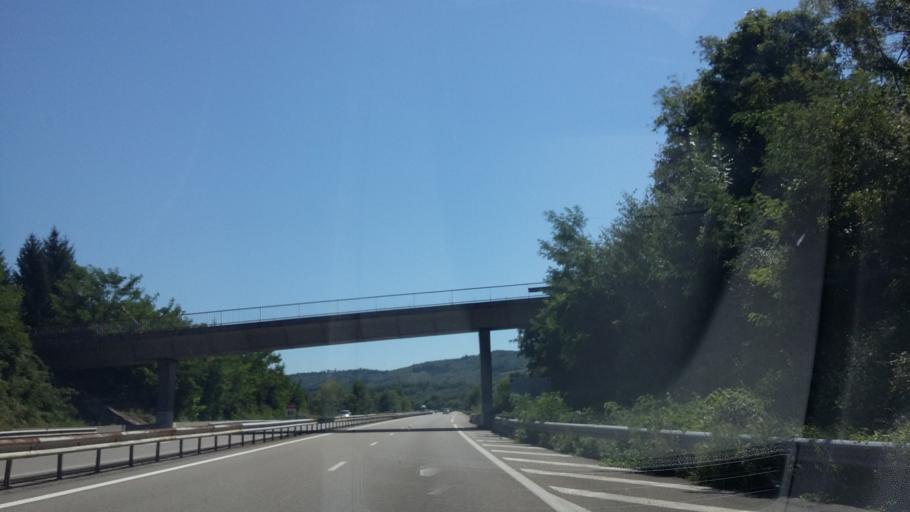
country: FR
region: Rhone-Alpes
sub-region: Departement de l'Isere
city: Chabons
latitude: 45.4346
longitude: 5.4209
